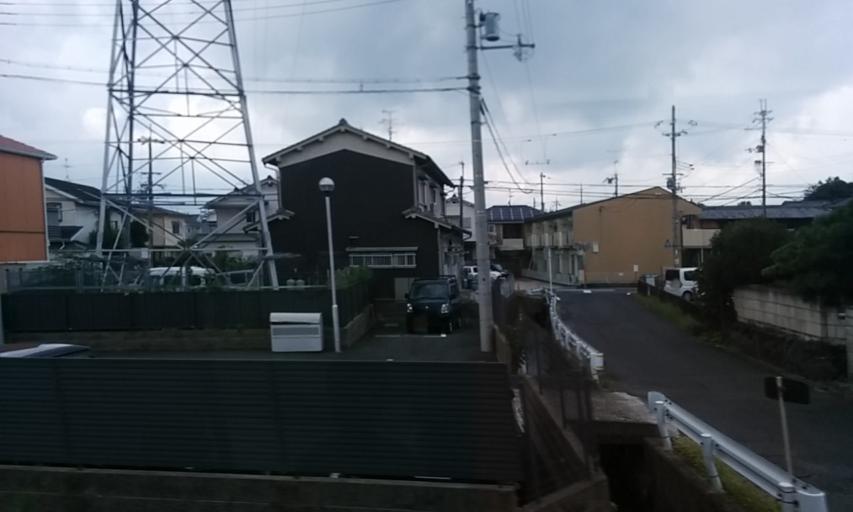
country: JP
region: Nara
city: Nara-shi
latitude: 34.6624
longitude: 135.7836
